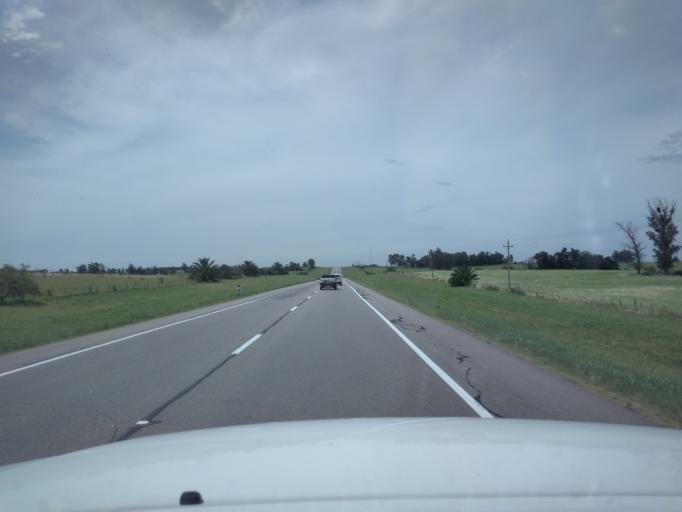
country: UY
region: Florida
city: Florida
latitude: -34.2205
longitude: -56.2089
